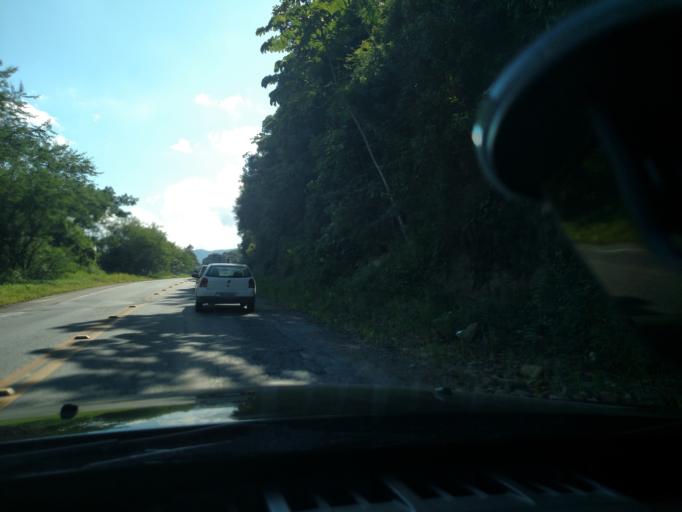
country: BR
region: Santa Catarina
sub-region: Ibirama
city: Ibirama
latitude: -27.0817
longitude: -49.5036
